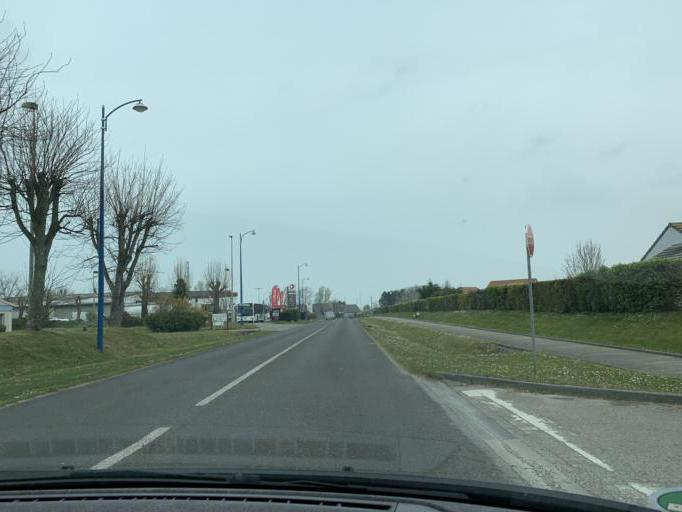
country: FR
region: Haute-Normandie
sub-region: Departement de la Seine-Maritime
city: Neville
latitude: 49.8592
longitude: 0.6959
